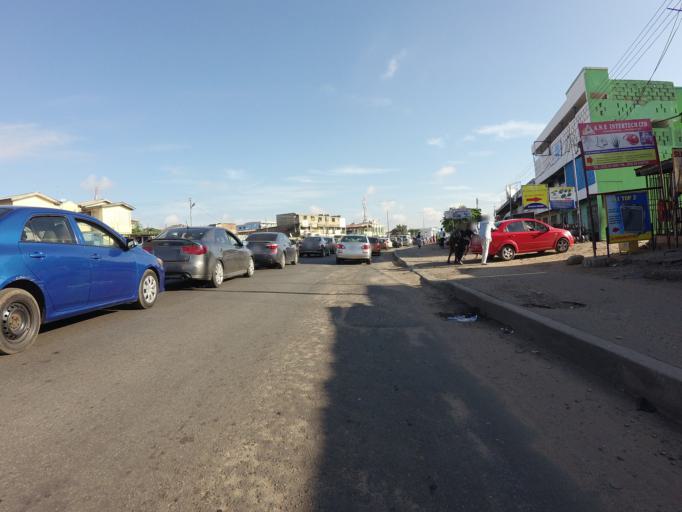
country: GH
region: Greater Accra
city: Accra
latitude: 5.5564
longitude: -0.2318
